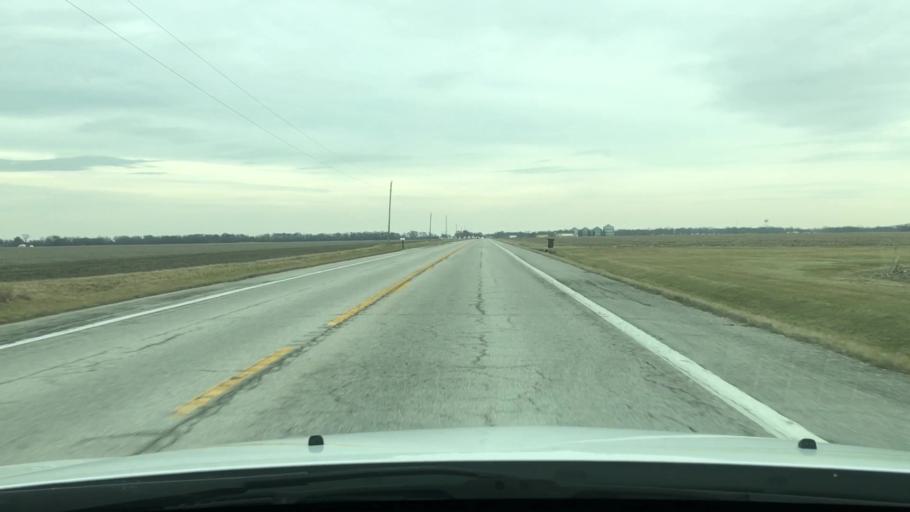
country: US
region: Missouri
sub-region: Audrain County
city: Vandalia
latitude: 39.2801
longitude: -91.6093
